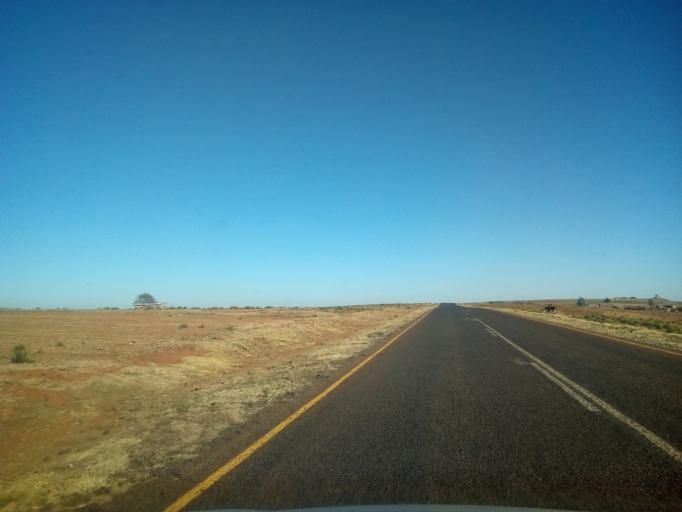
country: LS
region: Berea
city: Teyateyaneng
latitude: -29.2571
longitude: 27.7543
